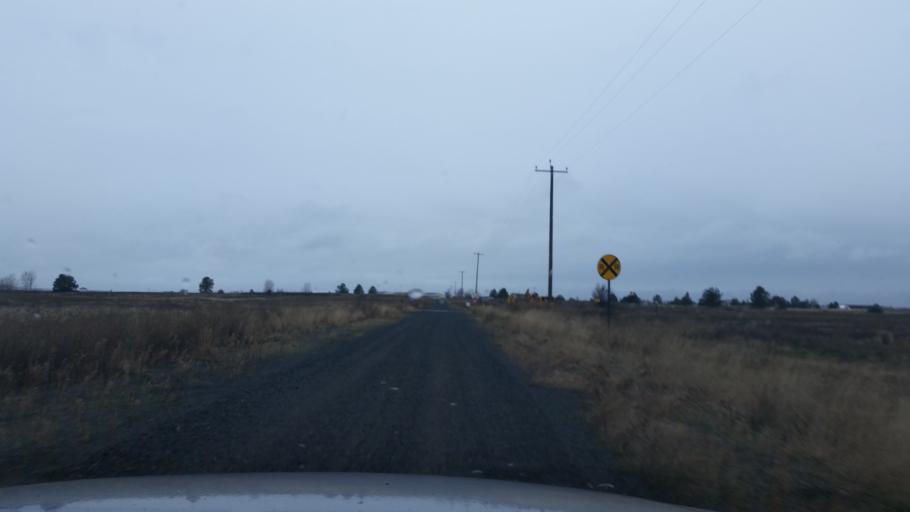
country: US
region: Washington
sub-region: Spokane County
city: Airway Heights
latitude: 47.6284
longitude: -117.6105
